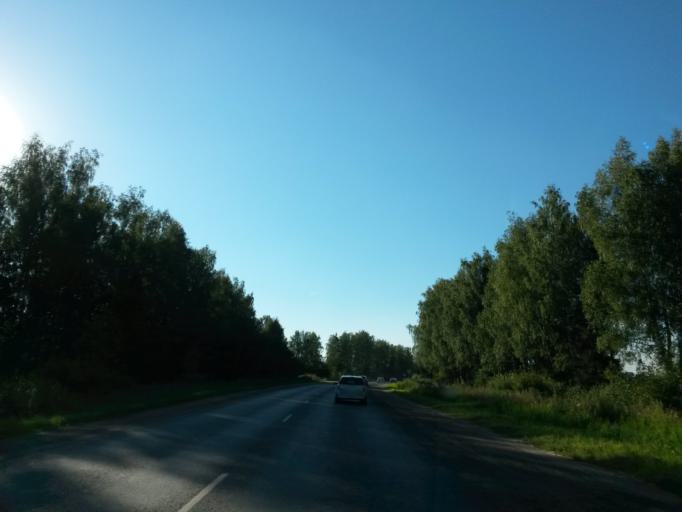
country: RU
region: Ivanovo
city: Novo-Talitsy
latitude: 57.0251
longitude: 40.7612
